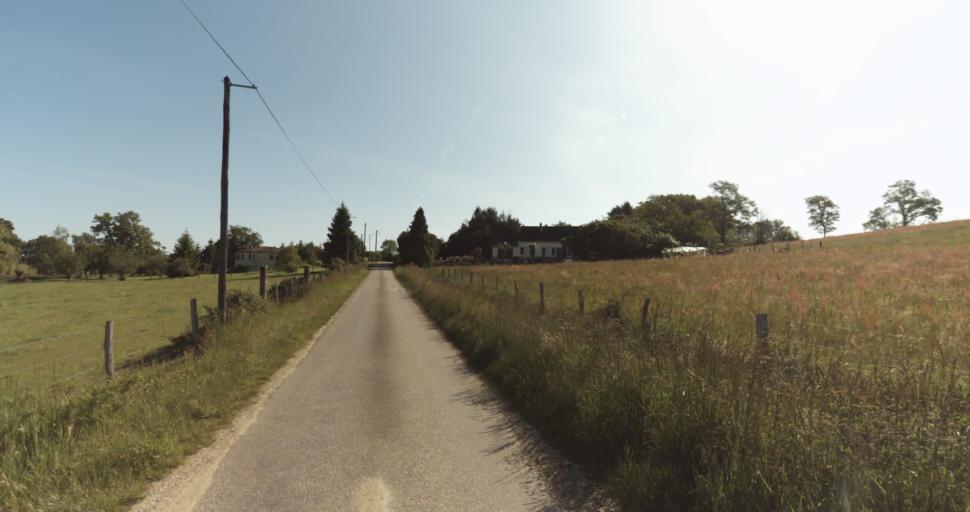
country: FR
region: Limousin
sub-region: Departement de la Haute-Vienne
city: Bosmie-l'Aiguille
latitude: 45.7244
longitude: 1.2372
